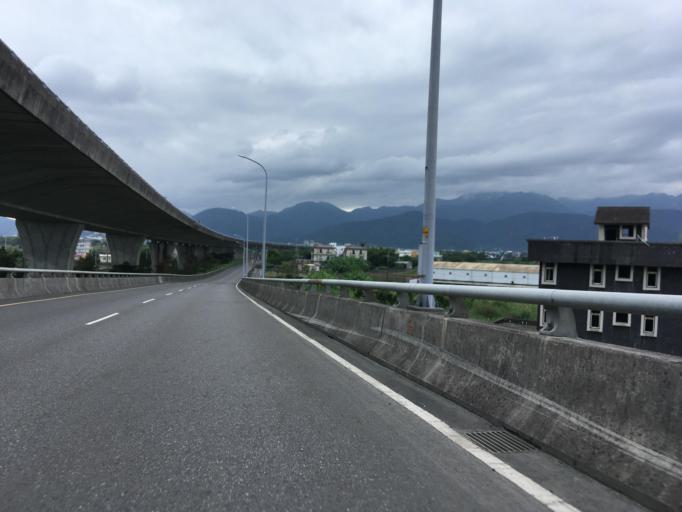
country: TW
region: Taiwan
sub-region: Yilan
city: Yilan
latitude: 24.6554
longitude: 121.8039
